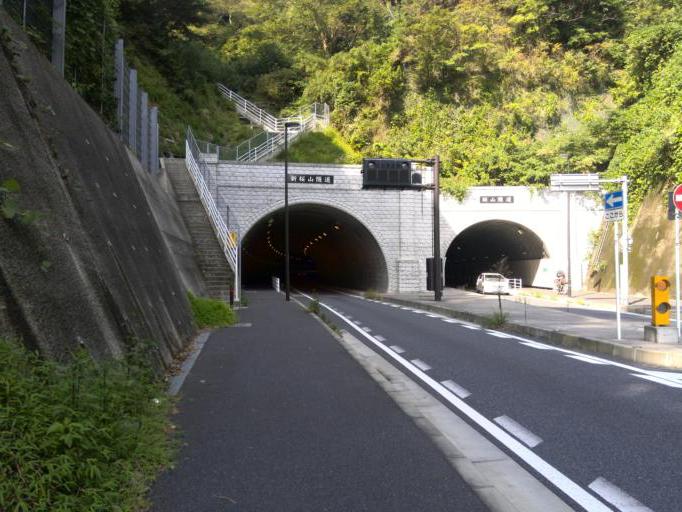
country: JP
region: Kanagawa
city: Zushi
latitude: 35.2855
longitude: 139.5803
